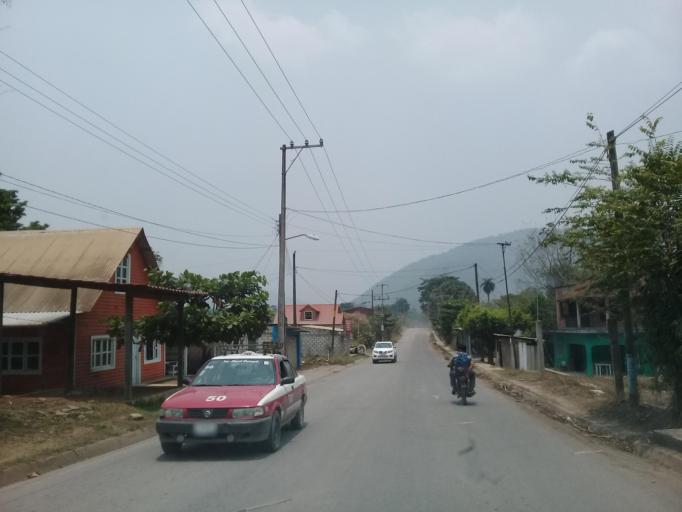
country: MX
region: Veracruz
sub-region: Tezonapa
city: Laguna Chica (Pueblo Nuevo)
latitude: 18.5472
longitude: -96.7306
